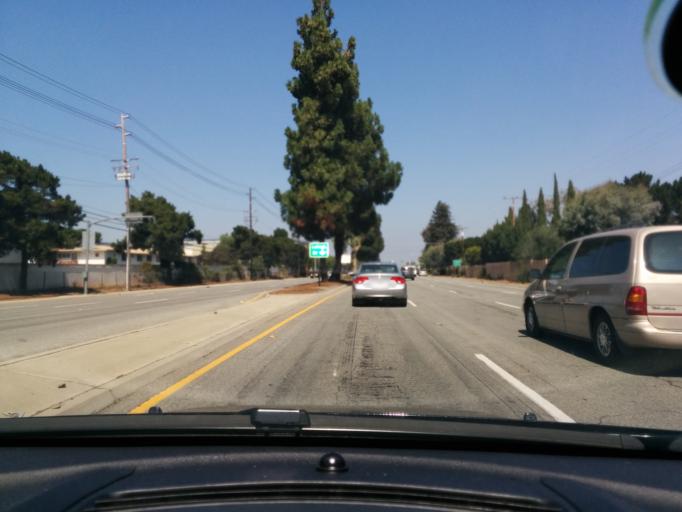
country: US
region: California
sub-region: Santa Clara County
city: Cupertino
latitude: 37.3325
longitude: -121.9955
